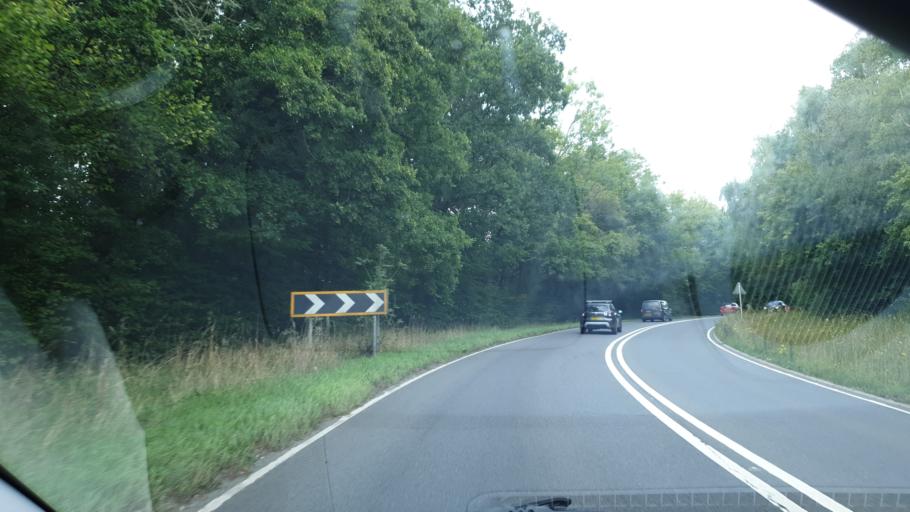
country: GB
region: England
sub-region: East Sussex
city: Forest Row
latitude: 51.1059
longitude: 0.0238
